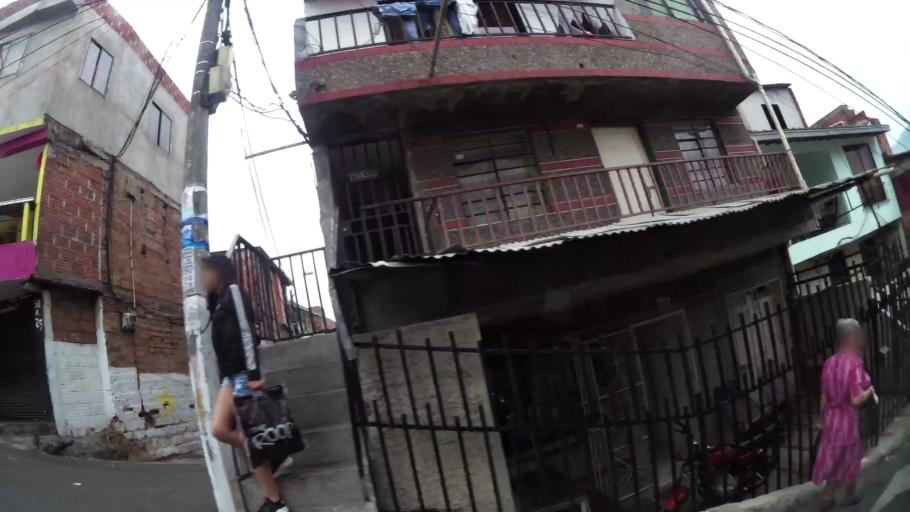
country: CO
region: Antioquia
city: Bello
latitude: 6.3048
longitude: -75.5532
